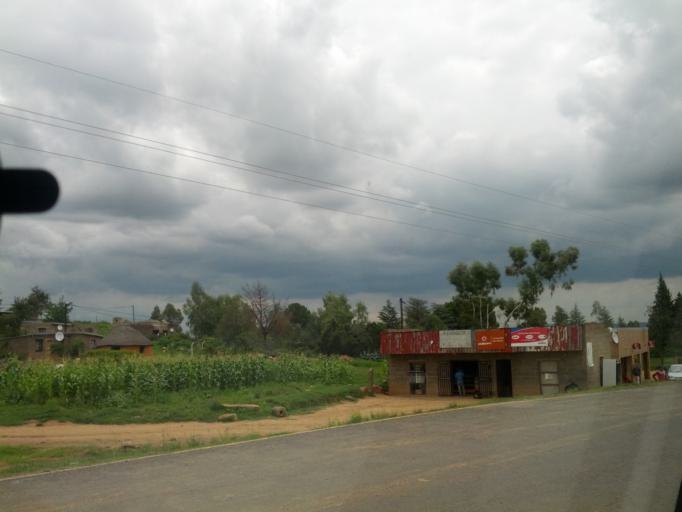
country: LS
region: Leribe
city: Leribe
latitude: -28.9260
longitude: 28.1308
